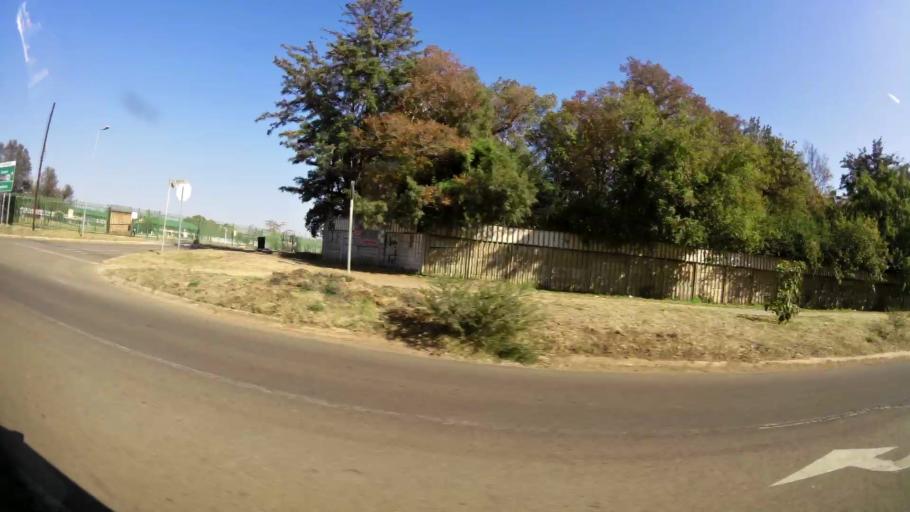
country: ZA
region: Gauteng
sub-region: City of Tshwane Metropolitan Municipality
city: Pretoria
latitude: -25.6637
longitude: 28.2439
